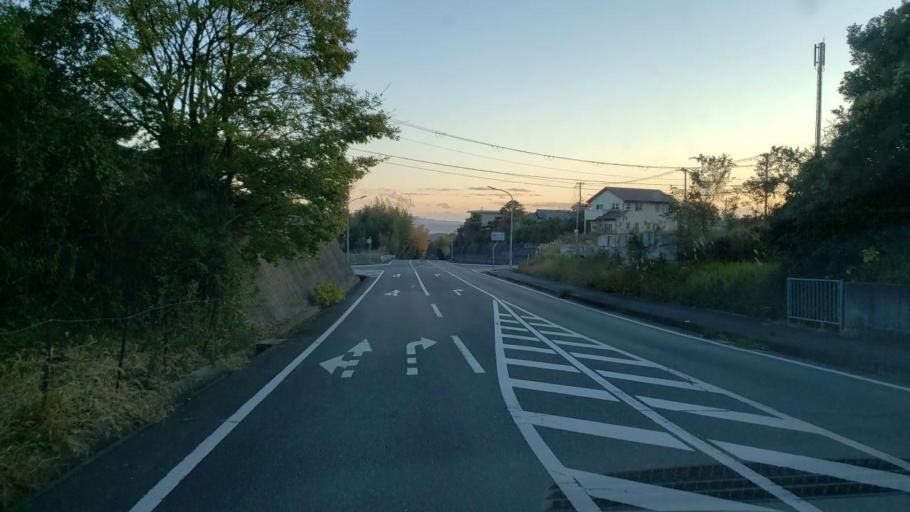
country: JP
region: Hyogo
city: Fukura
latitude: 34.3515
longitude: 134.7835
